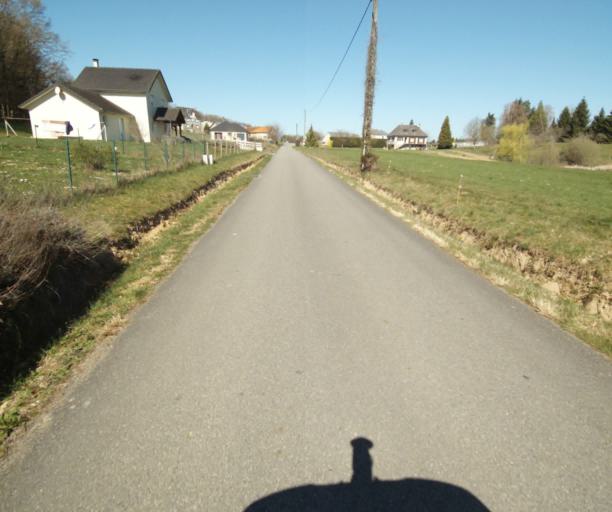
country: FR
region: Limousin
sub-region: Departement de la Correze
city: Saint-Clement
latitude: 45.3137
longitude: 1.6812
